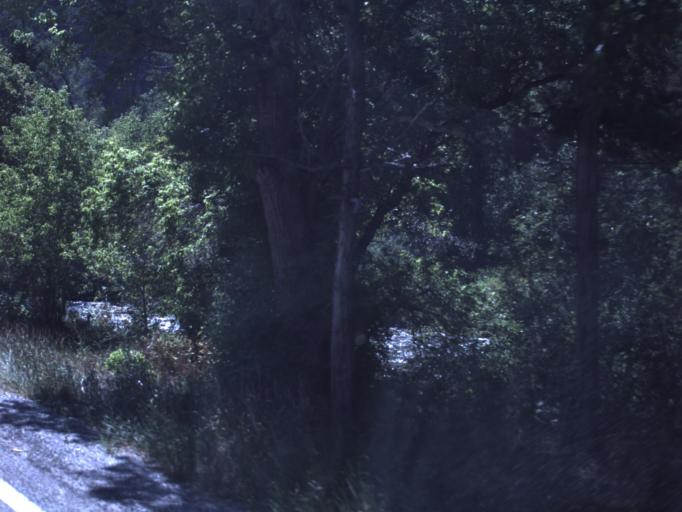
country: US
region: Utah
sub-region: Cache County
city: North Logan
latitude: 41.7904
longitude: -111.6458
